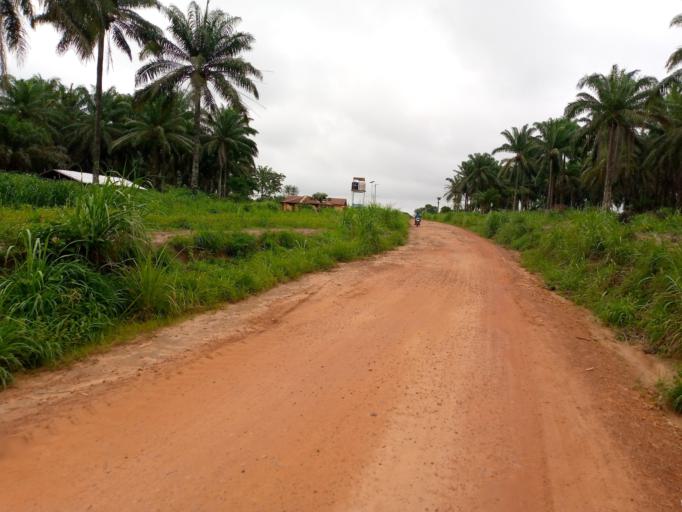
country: SL
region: Southern Province
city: Sumbuya
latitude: 7.5688
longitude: -12.0901
